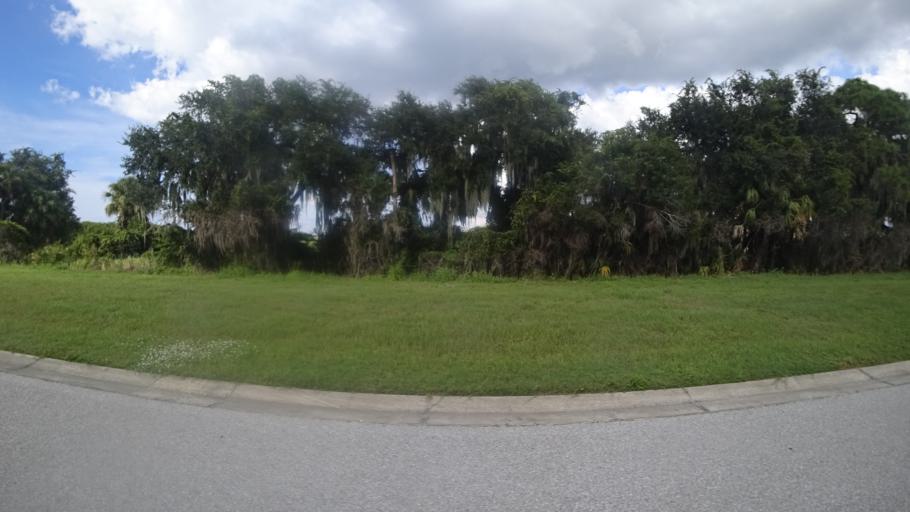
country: US
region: Florida
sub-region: Manatee County
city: Memphis
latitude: 27.6201
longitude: -82.5301
